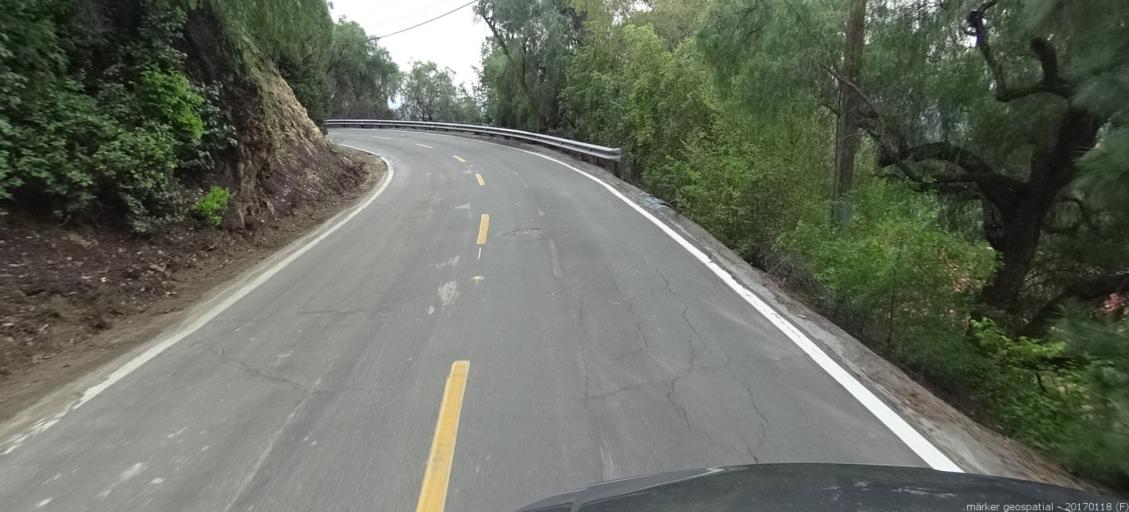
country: US
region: California
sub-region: Orange County
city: North Tustin
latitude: 33.7586
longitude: -117.7829
